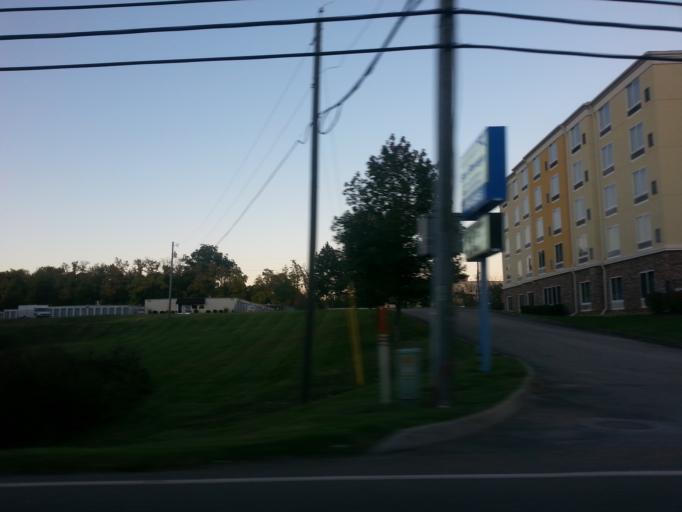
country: US
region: Tennessee
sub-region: Knox County
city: Knoxville
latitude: 36.0135
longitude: -83.9732
